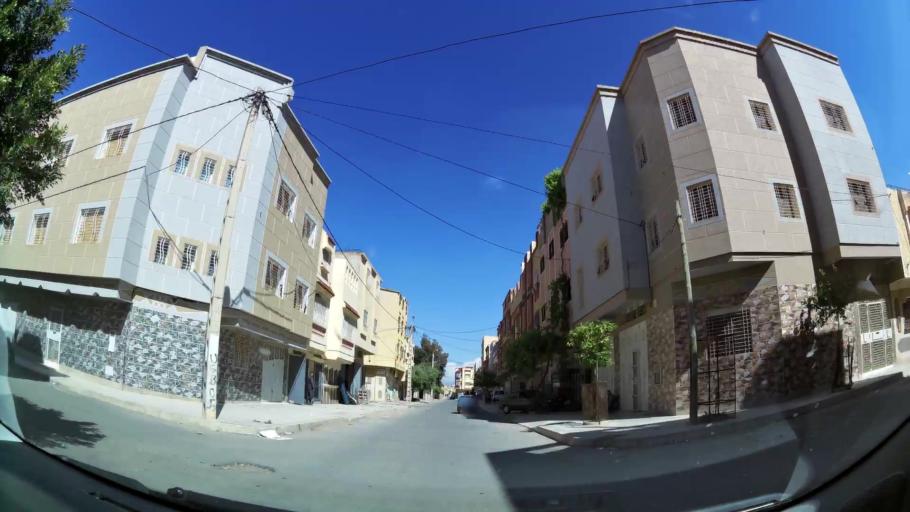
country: MA
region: Oriental
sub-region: Oujda-Angad
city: Oujda
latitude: 34.6855
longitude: -1.9399
